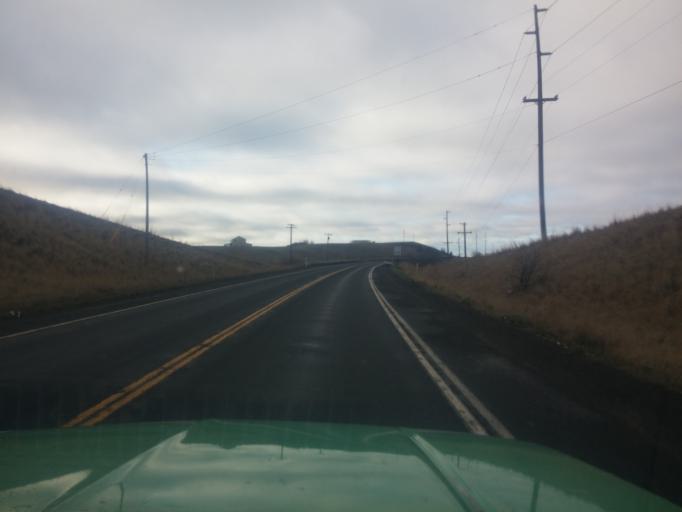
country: US
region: Idaho
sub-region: Latah County
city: Moscow
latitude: 46.8516
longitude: -117.0208
